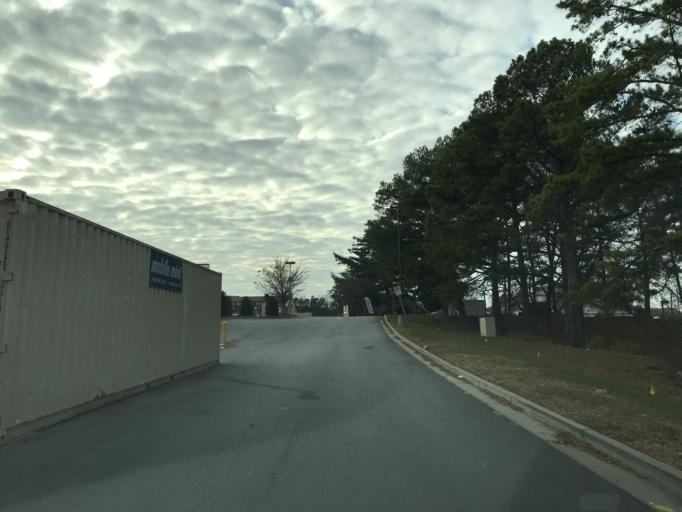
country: US
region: Georgia
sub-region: DeKalb County
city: Tucker
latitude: 33.8502
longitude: -84.2438
